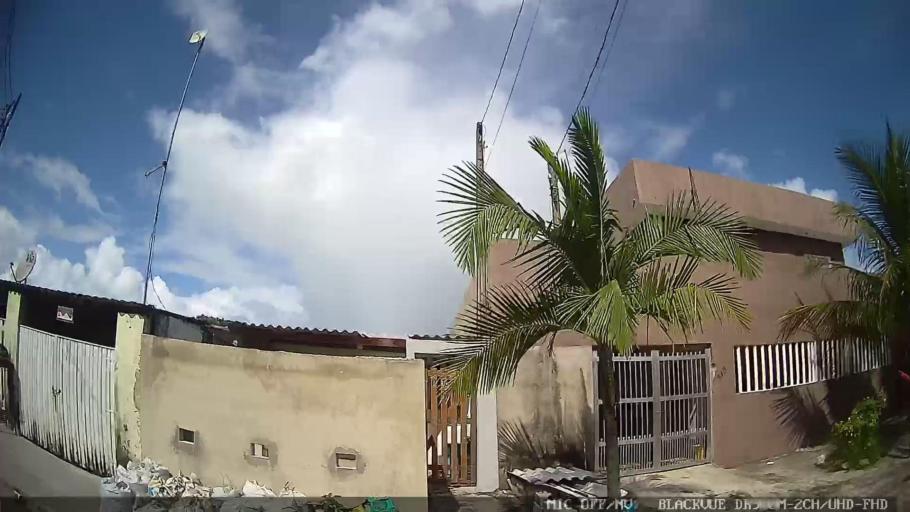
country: BR
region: Sao Paulo
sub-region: Itanhaem
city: Itanhaem
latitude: -24.2416
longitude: -46.8941
